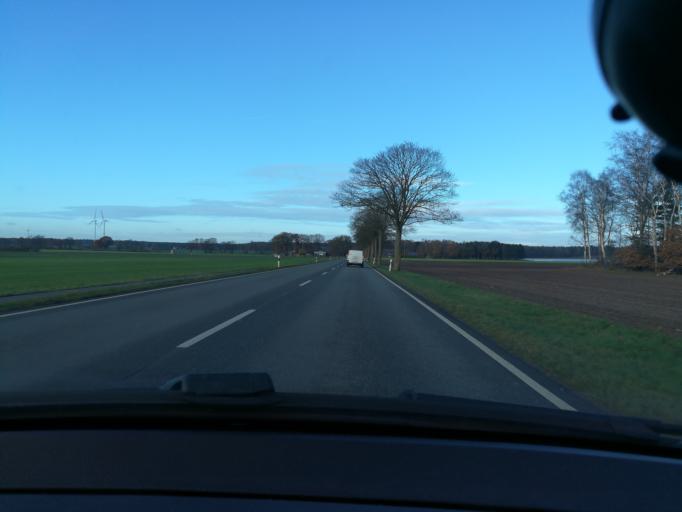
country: DE
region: Lower Saxony
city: Kirchdorf
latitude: 52.5557
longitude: 8.8584
